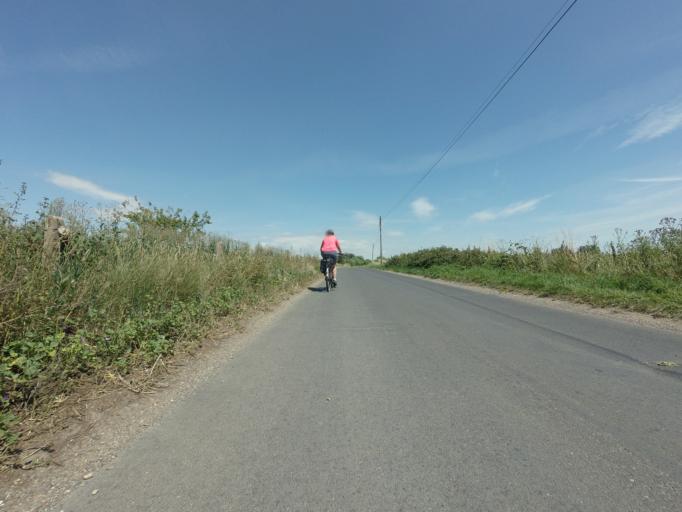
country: GB
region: England
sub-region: Kent
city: Lydd
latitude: 50.9863
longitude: 0.8869
